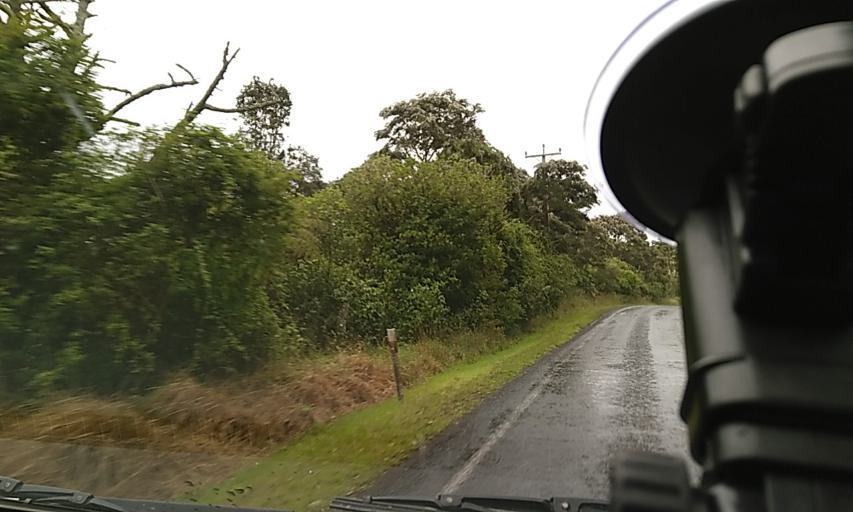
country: NZ
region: Auckland
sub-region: Auckland
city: Pukekohe East
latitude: -37.3011
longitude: 174.9376
